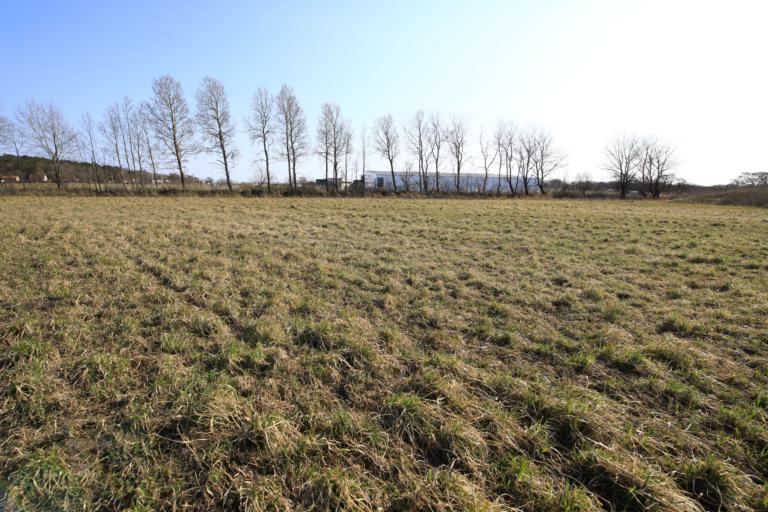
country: SE
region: Halland
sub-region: Varbergs Kommun
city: Varberg
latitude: 57.1403
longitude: 12.2762
